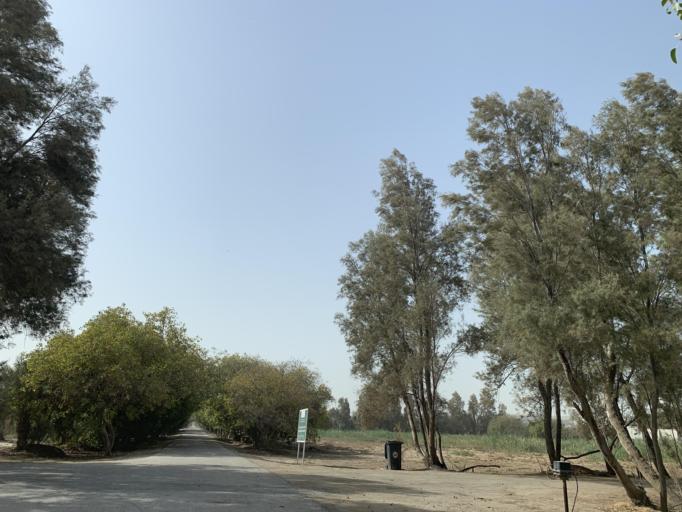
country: BH
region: Northern
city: Madinat `Isa
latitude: 26.1666
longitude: 50.5298
